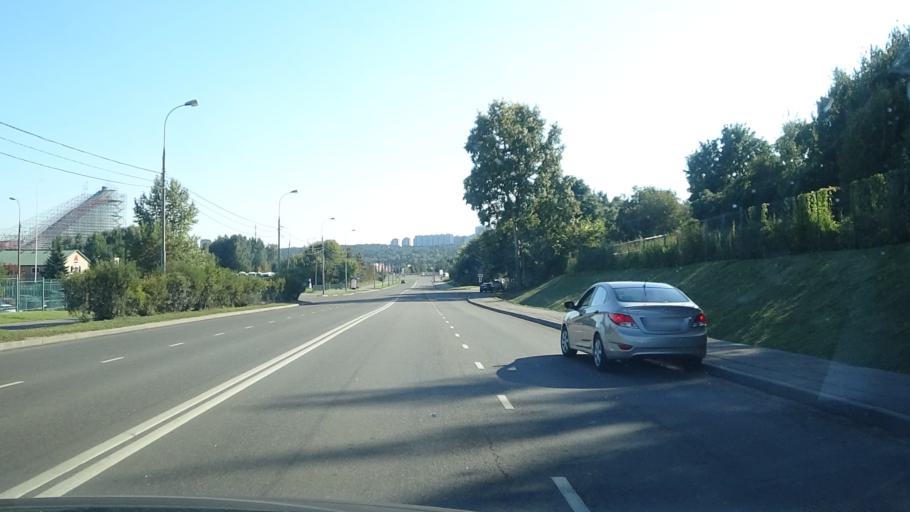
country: RU
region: Moscow
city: Shchukino
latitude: 55.7591
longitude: 37.4317
